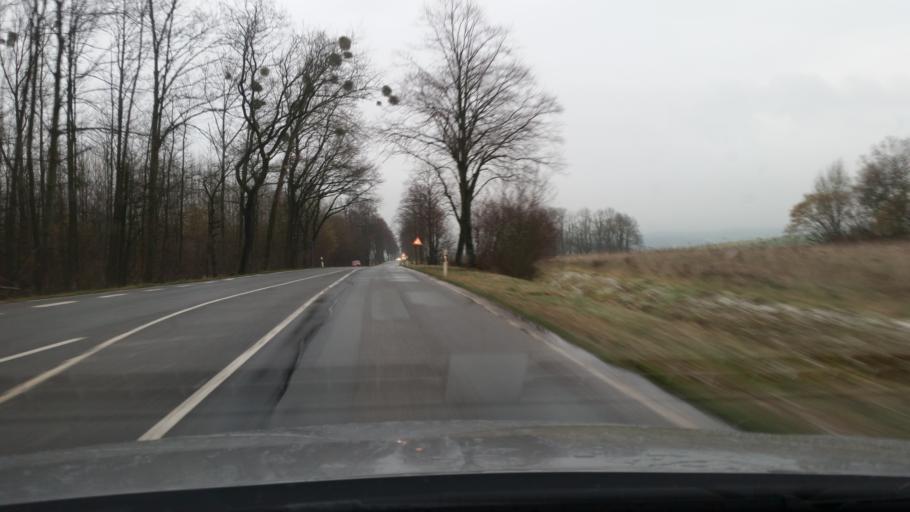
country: DE
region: Lower Saxony
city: Bad Munder am Deister
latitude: 52.1481
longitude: 9.4165
